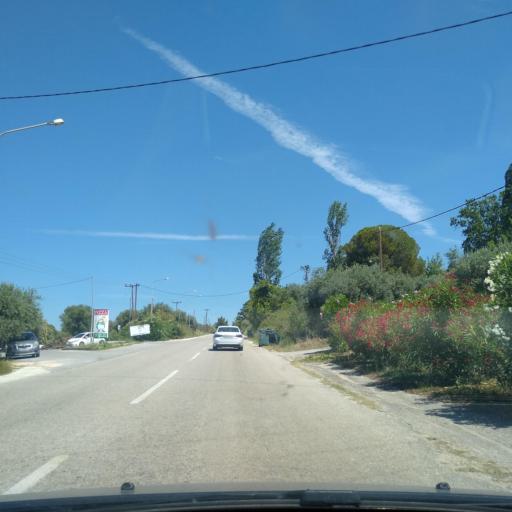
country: GR
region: Central Macedonia
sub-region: Nomos Chalkidikis
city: Neos Marmaras
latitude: 40.1823
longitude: 23.7993
